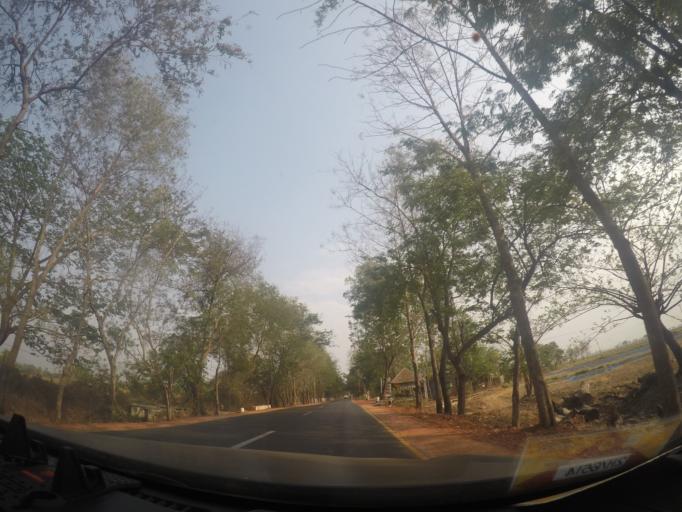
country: MM
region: Bago
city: Paungde
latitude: 18.3509
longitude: 95.6146
